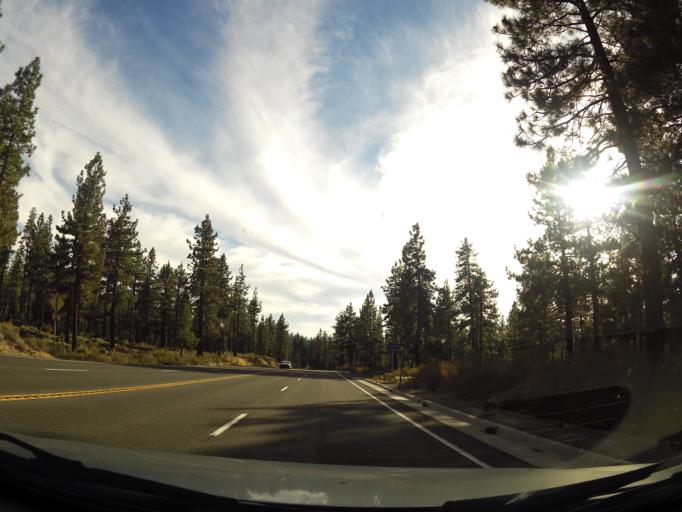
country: US
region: Nevada
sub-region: Douglas County
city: Kingsbury
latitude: 39.0189
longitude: -119.9464
